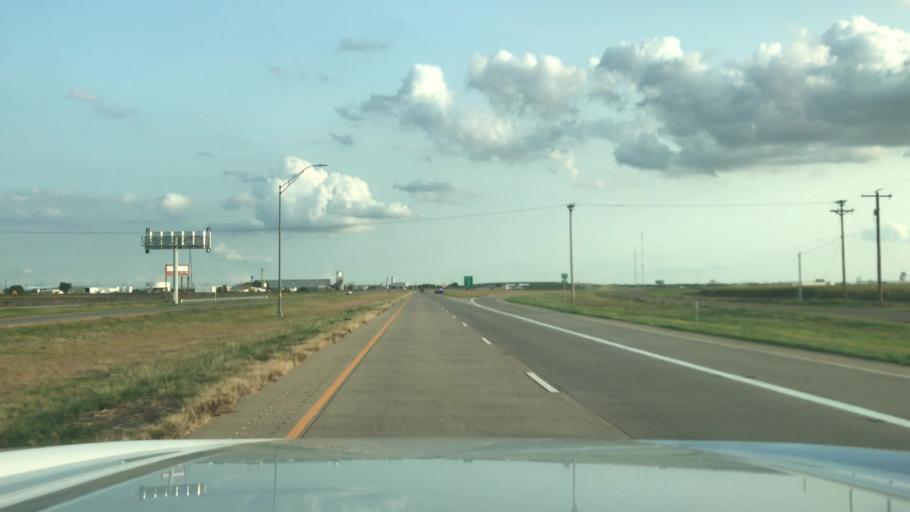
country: US
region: Texas
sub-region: Hale County
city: Seth Ward
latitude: 34.2423
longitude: -101.7088
